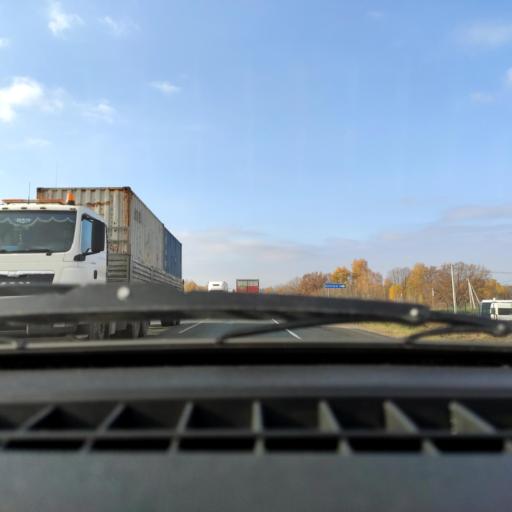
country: RU
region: Bashkortostan
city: Iglino
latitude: 54.7362
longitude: 56.2811
